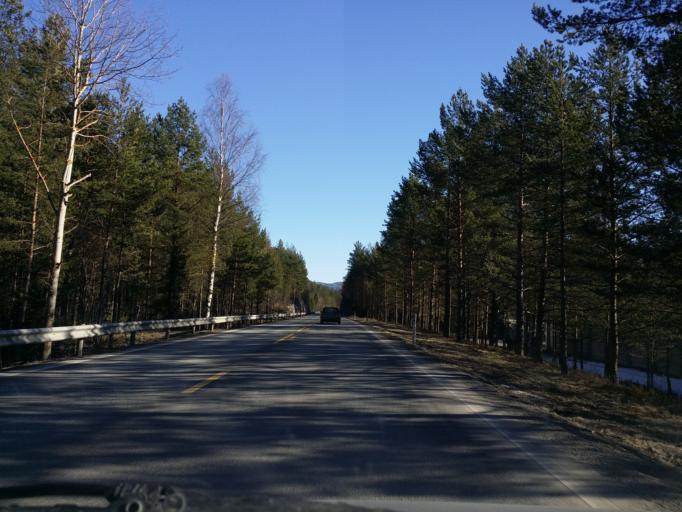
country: NO
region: Buskerud
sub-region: Ringerike
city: Honefoss
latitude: 60.2274
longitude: 10.2447
